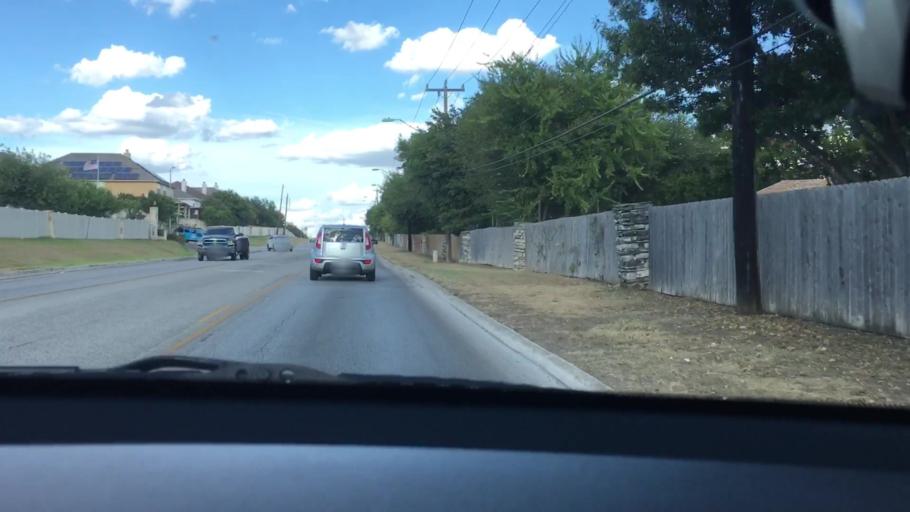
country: US
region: Texas
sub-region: Bexar County
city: Windcrest
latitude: 29.5200
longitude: -98.3673
